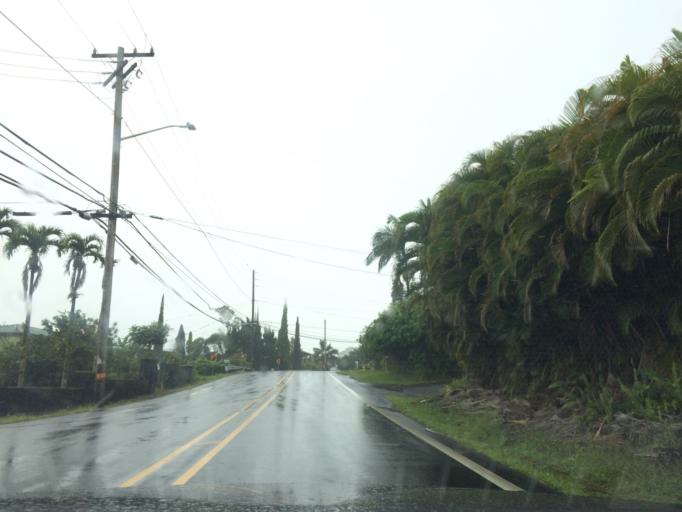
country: US
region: Hawaii
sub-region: Hawaii County
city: Hilo
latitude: 19.7001
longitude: -155.1145
